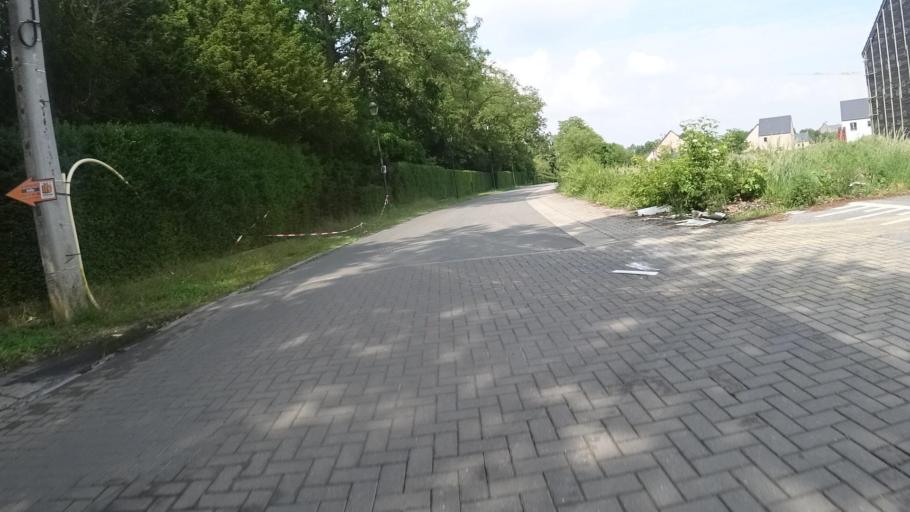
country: BE
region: Wallonia
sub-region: Province du Brabant Wallon
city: Wavre
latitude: 50.7034
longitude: 4.6261
